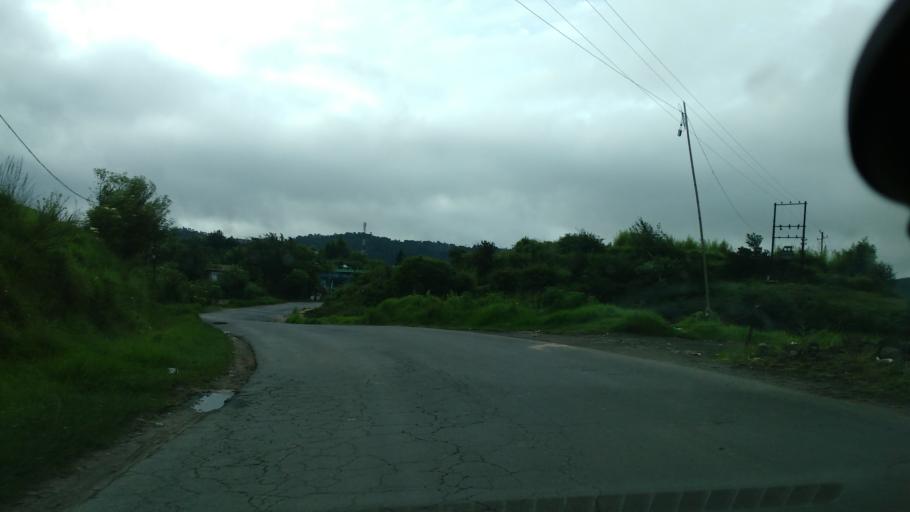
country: IN
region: Meghalaya
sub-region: East Khasi Hills
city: Shillong
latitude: 25.5043
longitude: 91.8143
